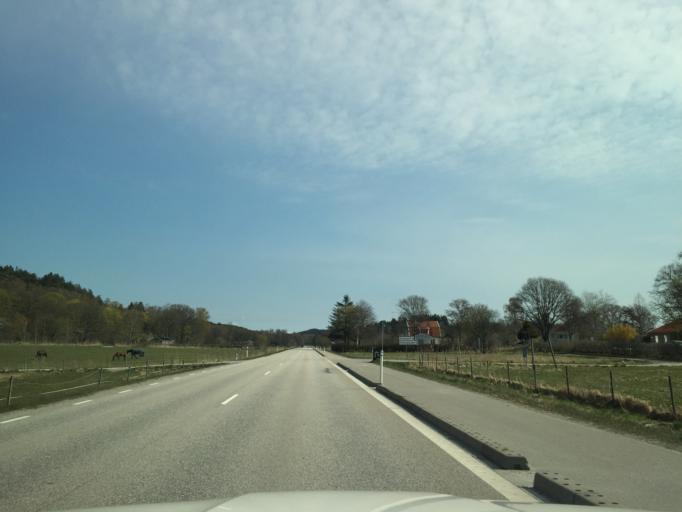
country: SE
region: Vaestra Goetaland
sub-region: Stenungsunds Kommun
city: Stora Hoga
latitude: 58.0338
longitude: 11.8787
